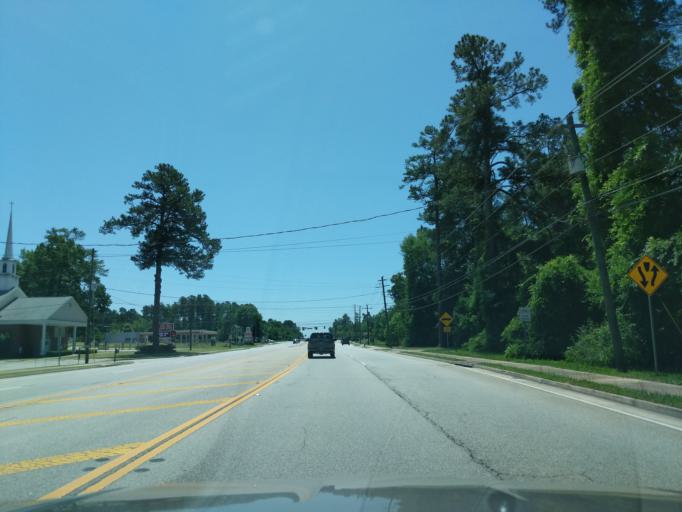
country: US
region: Georgia
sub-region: Columbia County
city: Martinez
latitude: 33.5521
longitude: -82.0914
